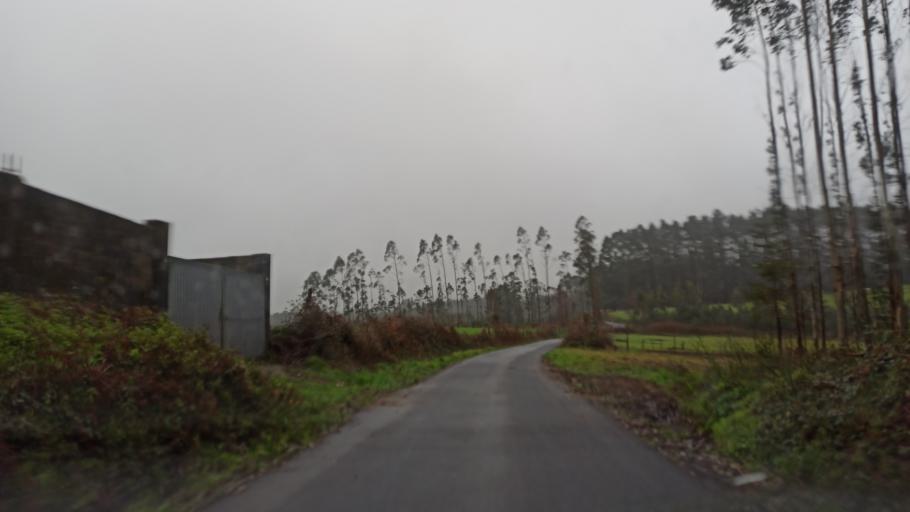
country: ES
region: Galicia
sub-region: Provincia da Coruna
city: Coiros
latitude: 43.1850
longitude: -8.1258
